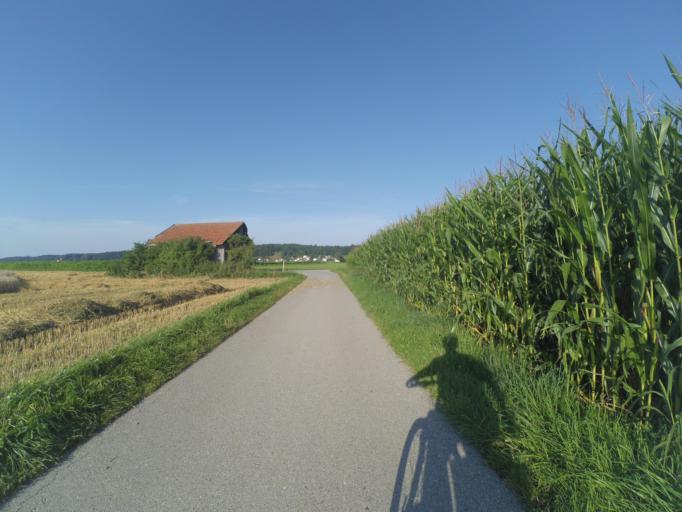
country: DE
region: Bavaria
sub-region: Swabia
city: Dirlewang
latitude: 48.0073
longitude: 10.5235
